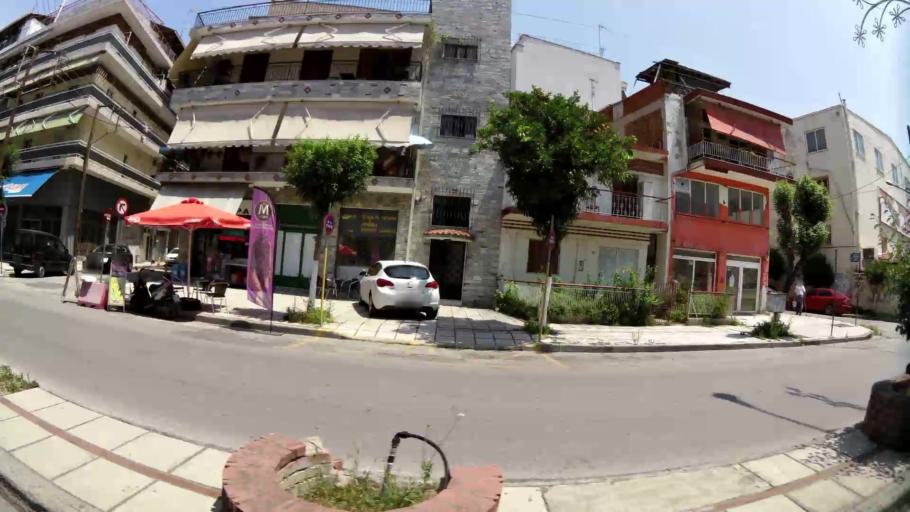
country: GR
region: Central Macedonia
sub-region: Nomos Thessalonikis
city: Ampelokipoi
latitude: 40.6564
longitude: 22.9273
